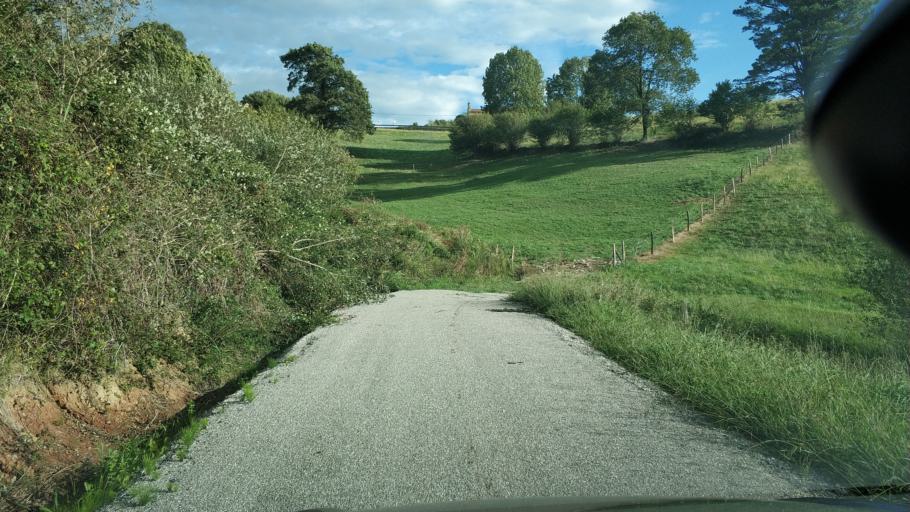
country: ES
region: Cantabria
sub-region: Provincia de Cantabria
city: Santa Maria de Cayon
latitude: 43.2864
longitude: -3.8133
